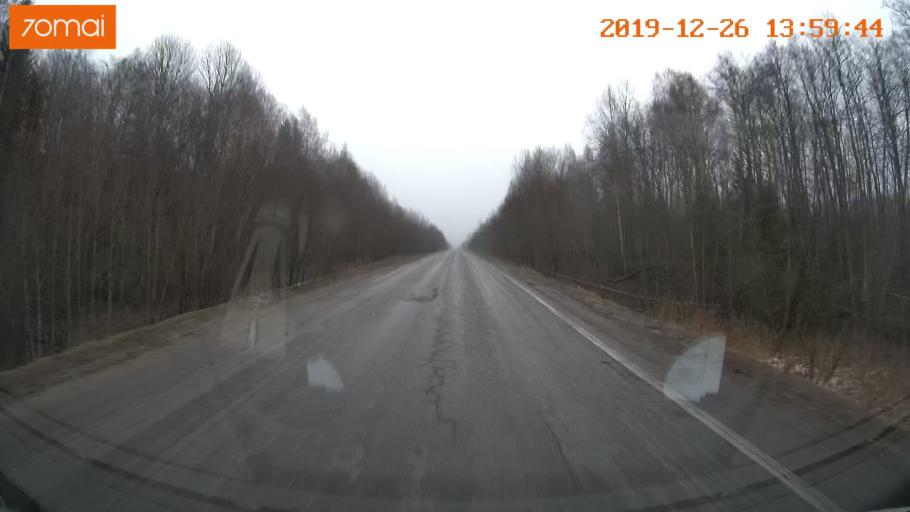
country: RU
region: Jaroslavl
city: Poshekhon'ye
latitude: 58.5633
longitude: 38.7296
